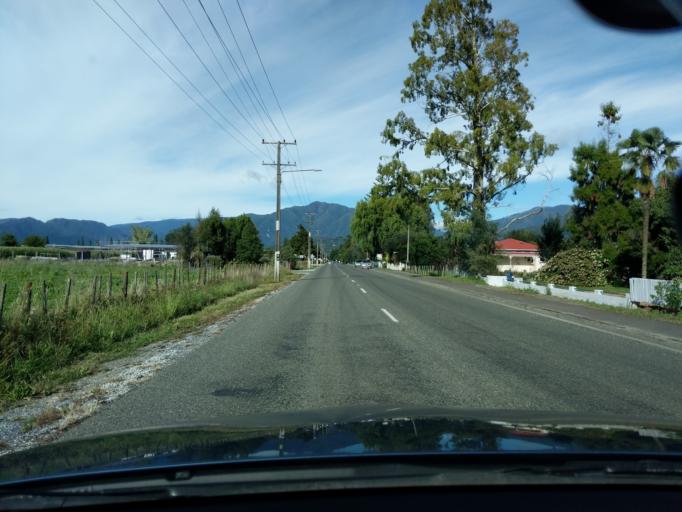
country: NZ
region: Tasman
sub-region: Tasman District
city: Takaka
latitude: -40.8566
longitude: 172.8125
